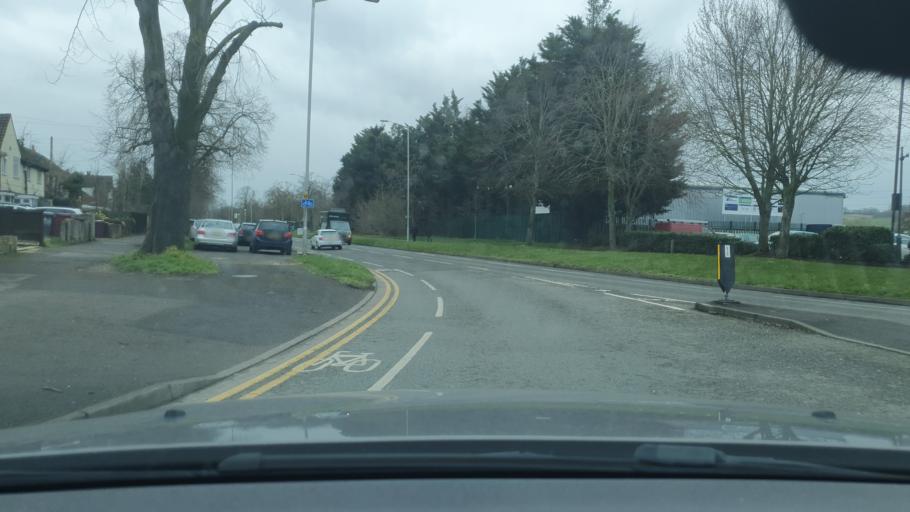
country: GB
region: England
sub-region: West Berkshire
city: Tilehurst
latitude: 51.4662
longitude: -1.0213
